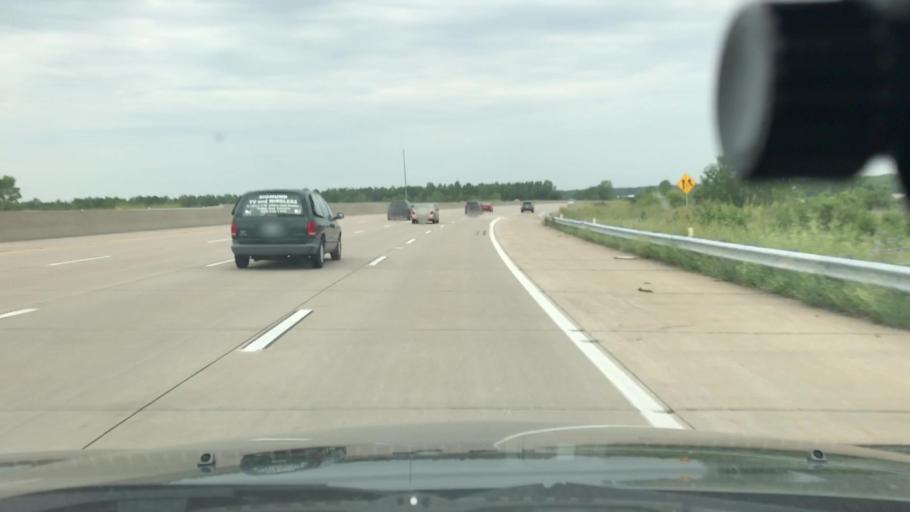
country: US
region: Missouri
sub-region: Saint Louis County
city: Maryland Heights
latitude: 38.7074
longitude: -90.5002
